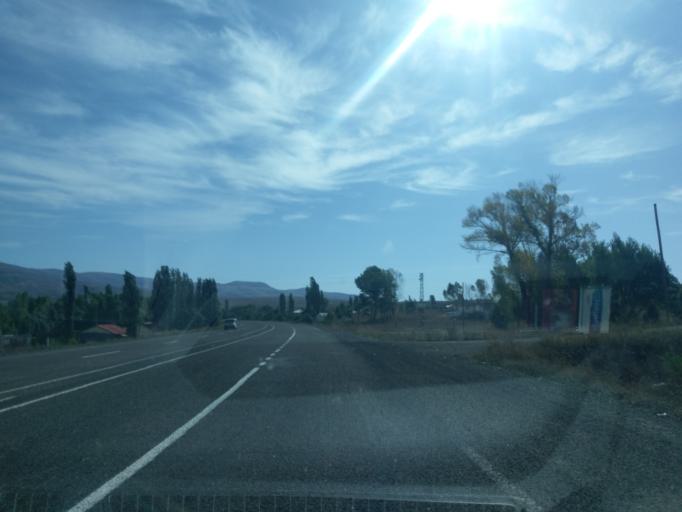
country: TR
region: Sivas
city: Imranli
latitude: 39.8360
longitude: 38.2605
